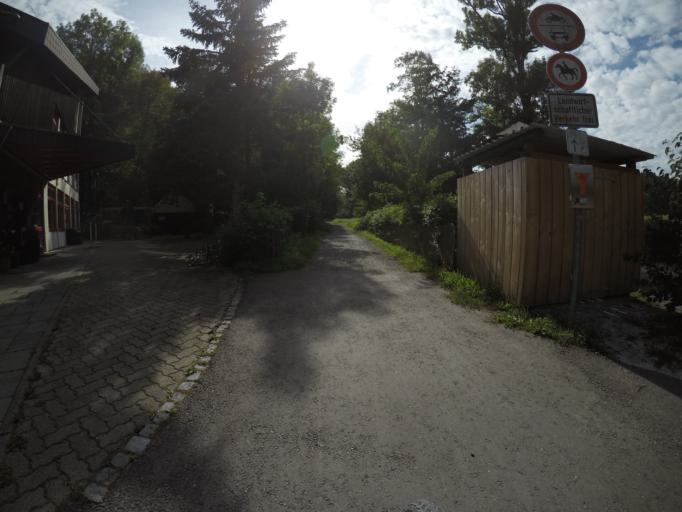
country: DE
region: Baden-Wuerttemberg
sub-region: Regierungsbezirk Stuttgart
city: Eberdingen
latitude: 48.8919
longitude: 8.9674
